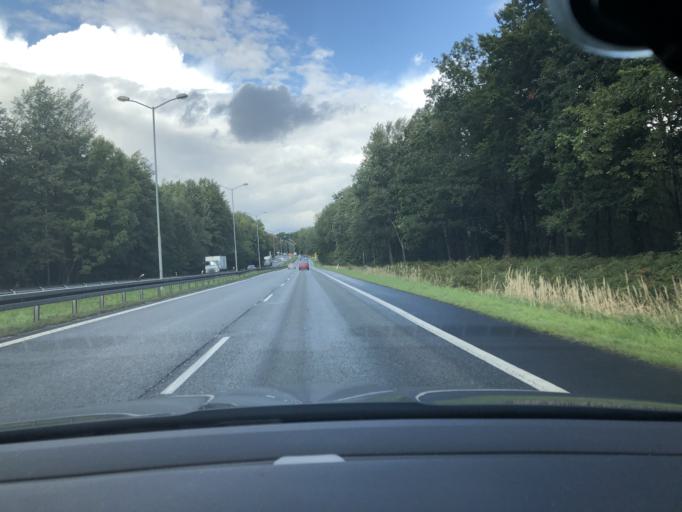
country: PL
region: Silesian Voivodeship
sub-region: Katowice
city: Murcki
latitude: 50.2121
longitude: 19.0560
